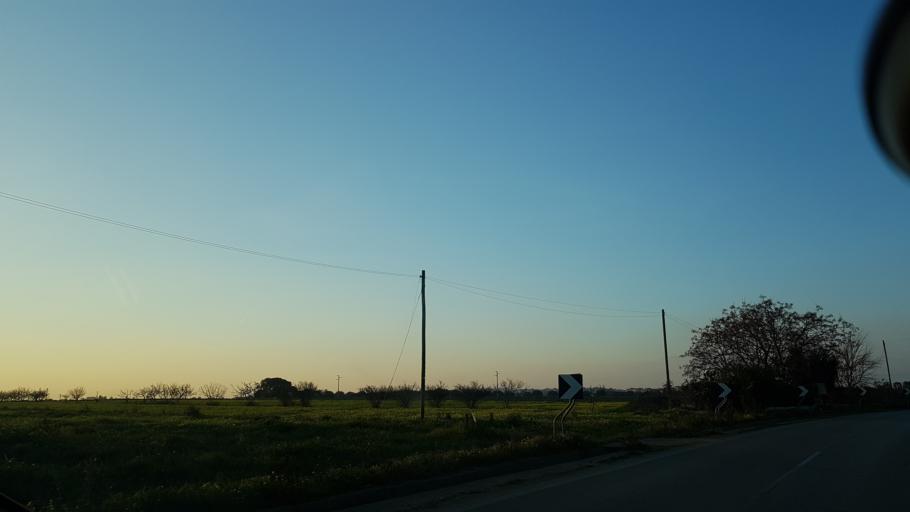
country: IT
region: Apulia
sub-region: Provincia di Brindisi
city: La Rosa
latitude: 40.6055
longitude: 17.9453
